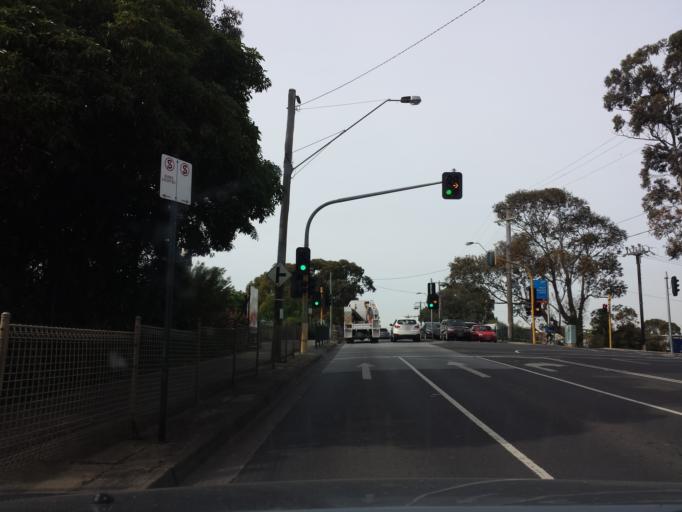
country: AU
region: Victoria
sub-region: Monash
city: Ashwood
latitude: -37.8747
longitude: 145.1292
